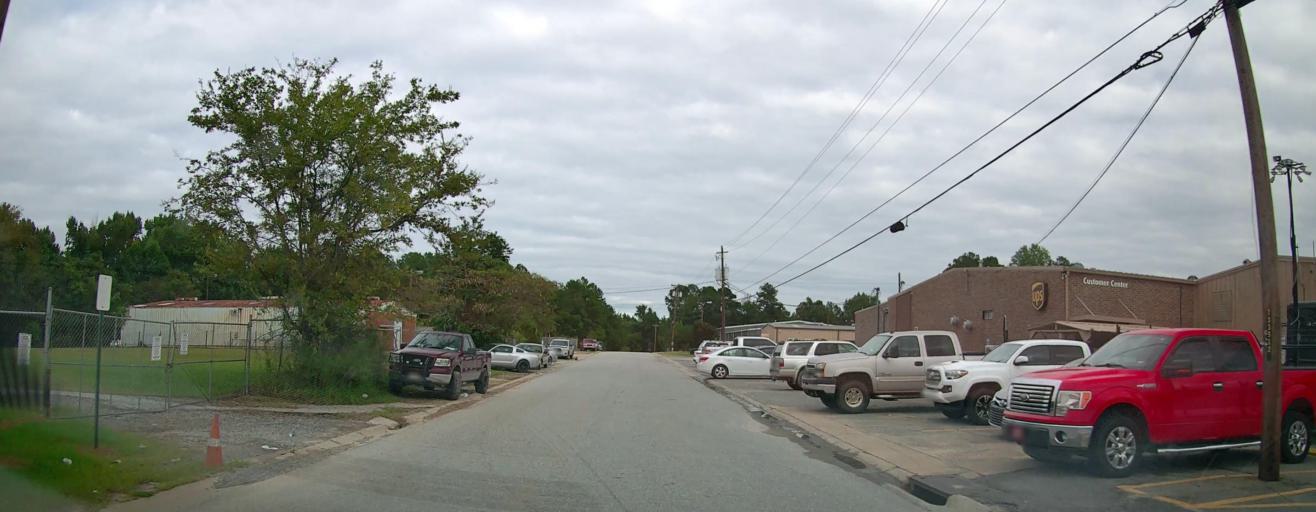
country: US
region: Georgia
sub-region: Bibb County
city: Macon
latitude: 32.8131
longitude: -83.6312
